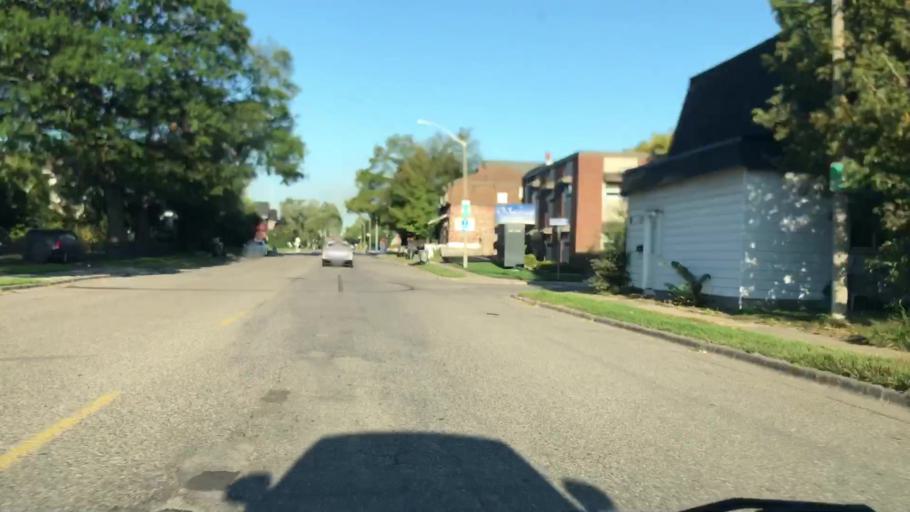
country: CA
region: Ontario
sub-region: Algoma
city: Sault Ste. Marie
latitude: 46.5207
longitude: -84.3455
